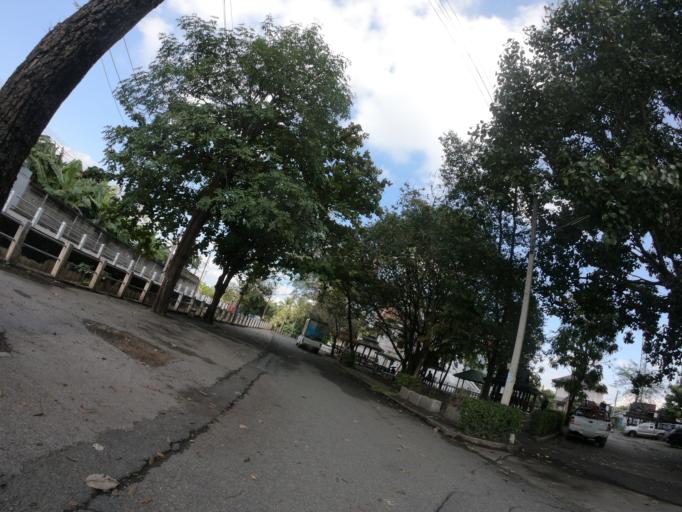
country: TH
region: Chiang Mai
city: Chiang Mai
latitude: 18.7867
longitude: 99.0322
